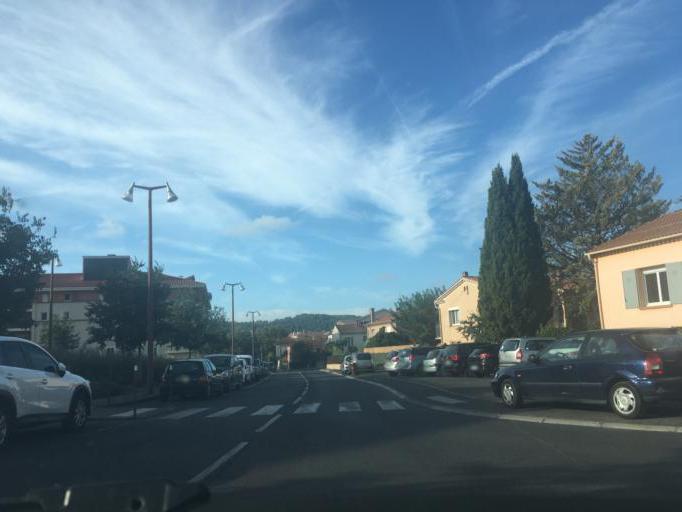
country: FR
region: Provence-Alpes-Cote d'Azur
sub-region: Departement du Var
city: Draguignan
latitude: 43.5343
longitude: 6.4729
